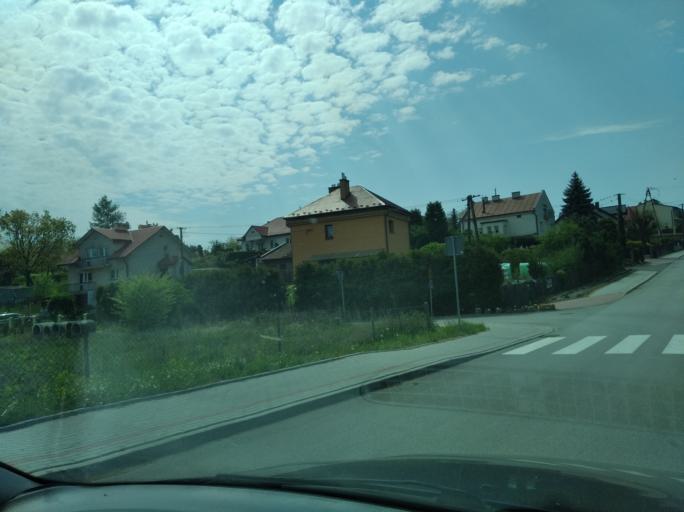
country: PL
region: Subcarpathian Voivodeship
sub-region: Powiat jaroslawski
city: Jaroslaw
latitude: 50.0054
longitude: 22.6818
